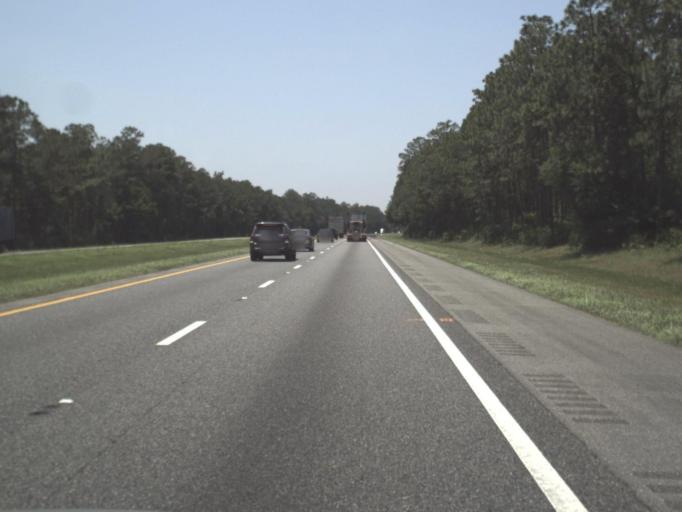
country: US
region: Florida
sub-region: Columbia County
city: Watertown
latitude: 30.2540
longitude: -82.4194
